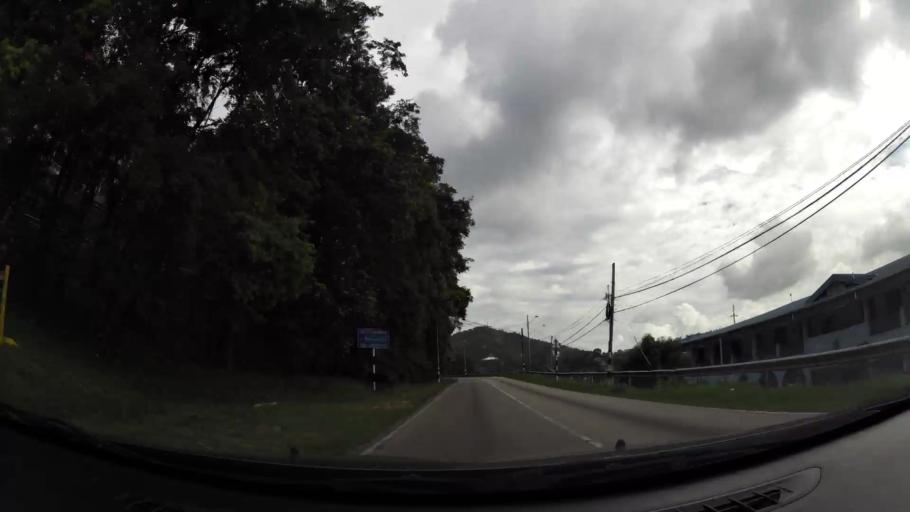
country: TT
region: City of Port of Spain
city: Port-of-Spain
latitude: 10.6706
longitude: -61.5091
